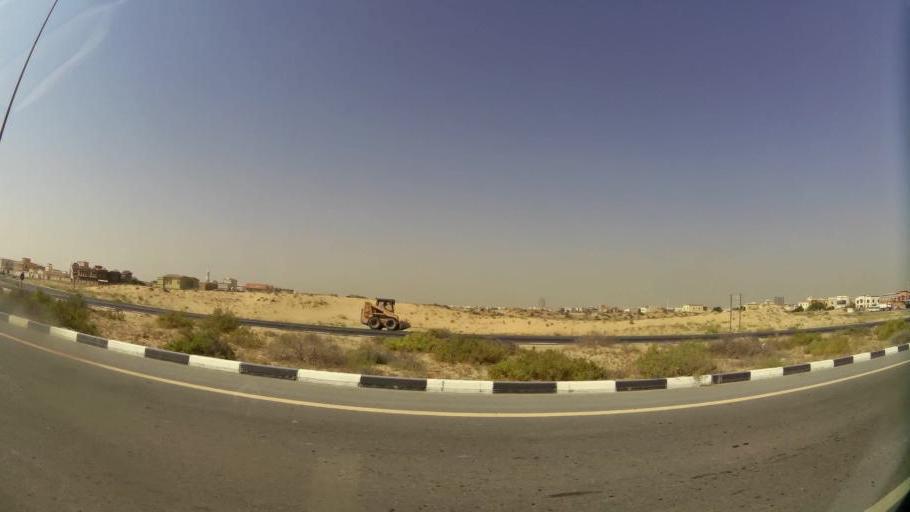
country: AE
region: Ajman
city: Ajman
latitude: 25.4220
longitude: 55.5326
